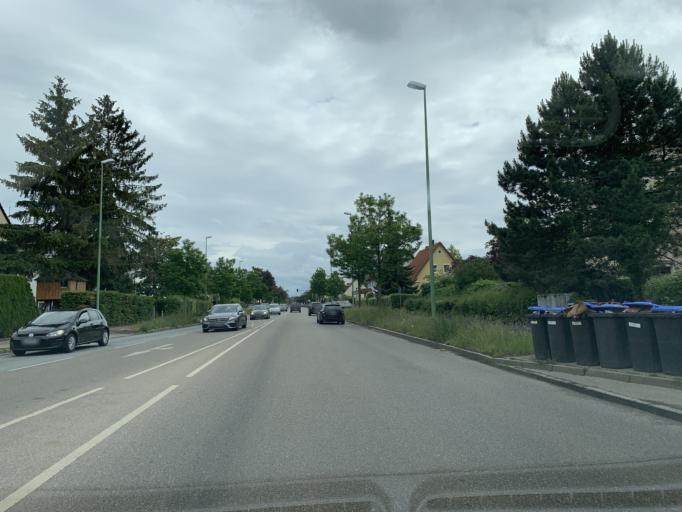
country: DE
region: Bavaria
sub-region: Swabia
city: Neu-Ulm
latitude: 48.3704
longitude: 10.0085
